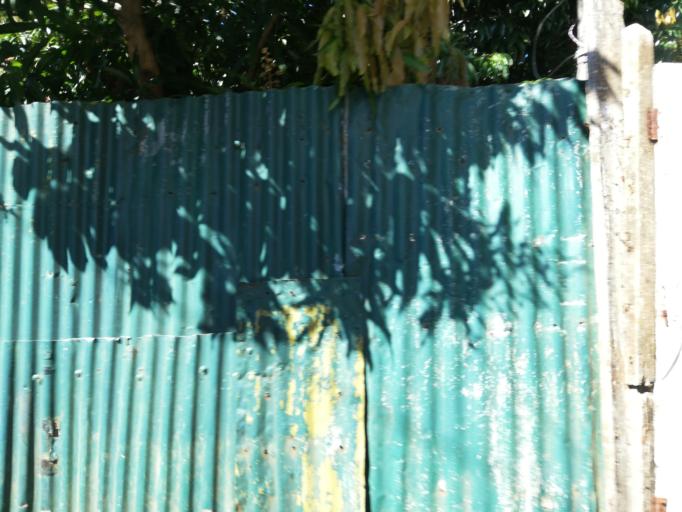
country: MU
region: Moka
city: Moka
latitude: -20.2199
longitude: 57.4674
